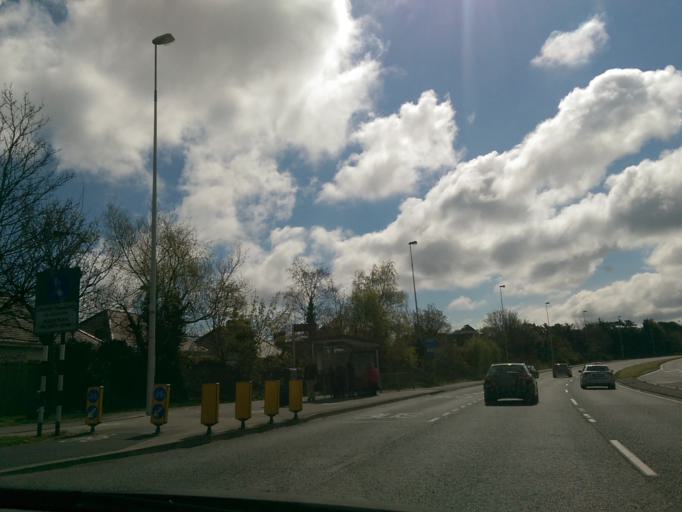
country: IE
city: Booterstown
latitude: 53.2892
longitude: -6.1952
